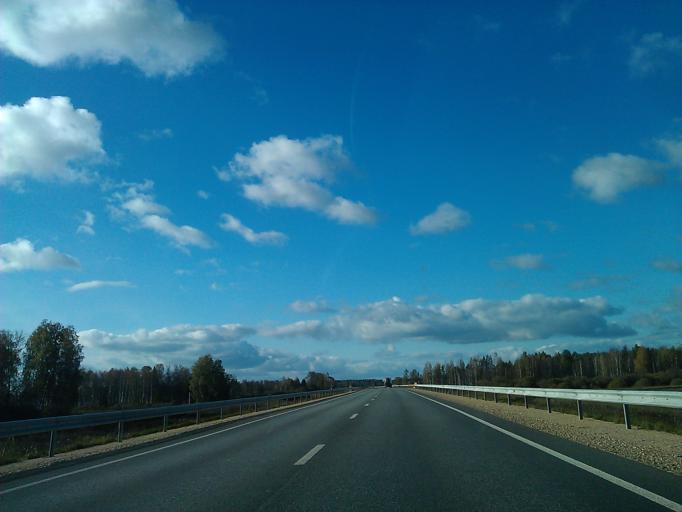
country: LV
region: Koknese
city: Koknese
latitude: 56.6801
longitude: 25.3853
